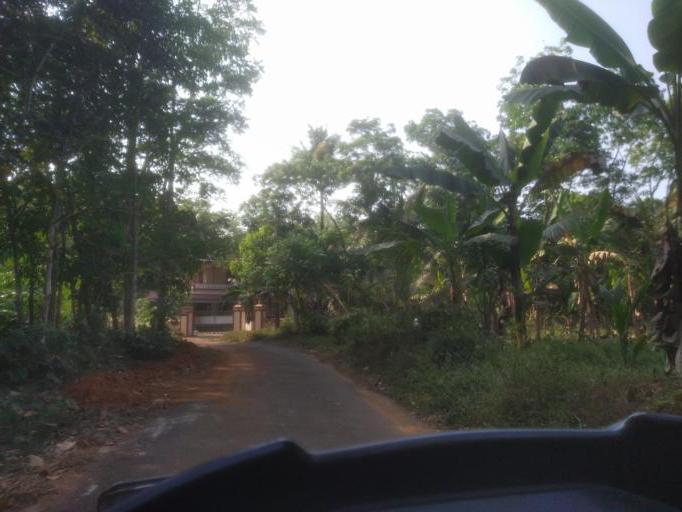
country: IN
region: Kerala
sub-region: Ernakulam
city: Piravam
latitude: 9.8771
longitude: 76.5507
